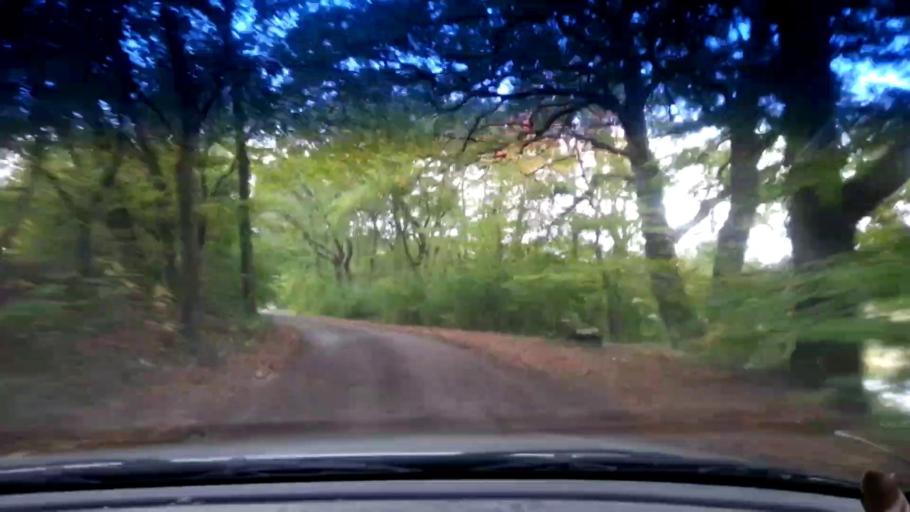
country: DE
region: Bavaria
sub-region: Upper Franconia
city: Priesendorf
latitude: 49.8941
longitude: 10.7205
